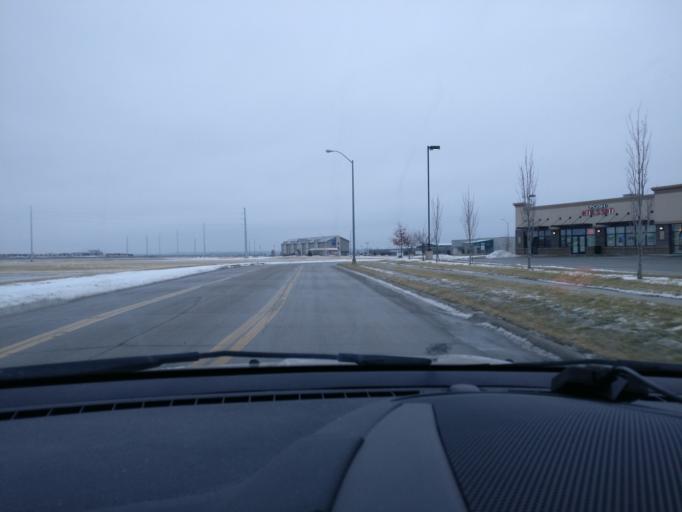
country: US
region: Nebraska
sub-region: Dodge County
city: Fremont
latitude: 41.4519
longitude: -96.4551
